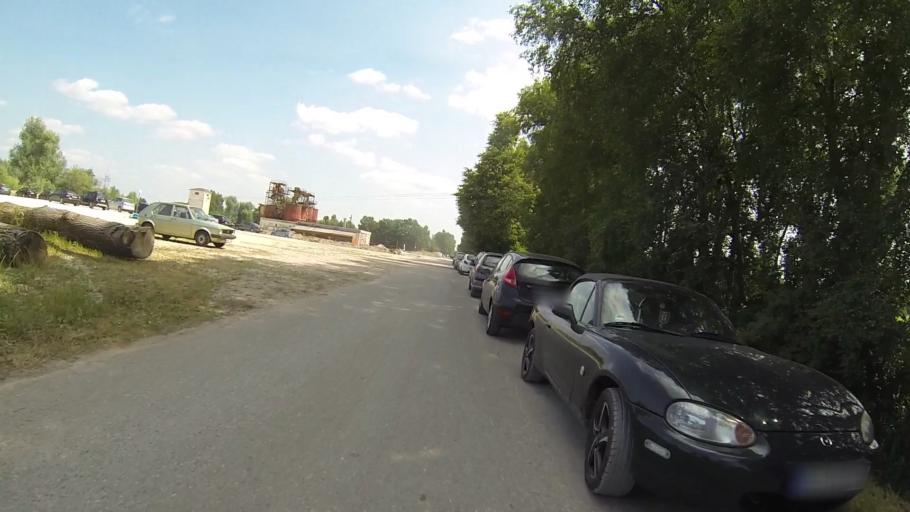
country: DE
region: Baden-Wuerttemberg
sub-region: Regierungsbezirk Stuttgart
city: Niederstotzingen
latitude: 48.5032
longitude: 10.2648
